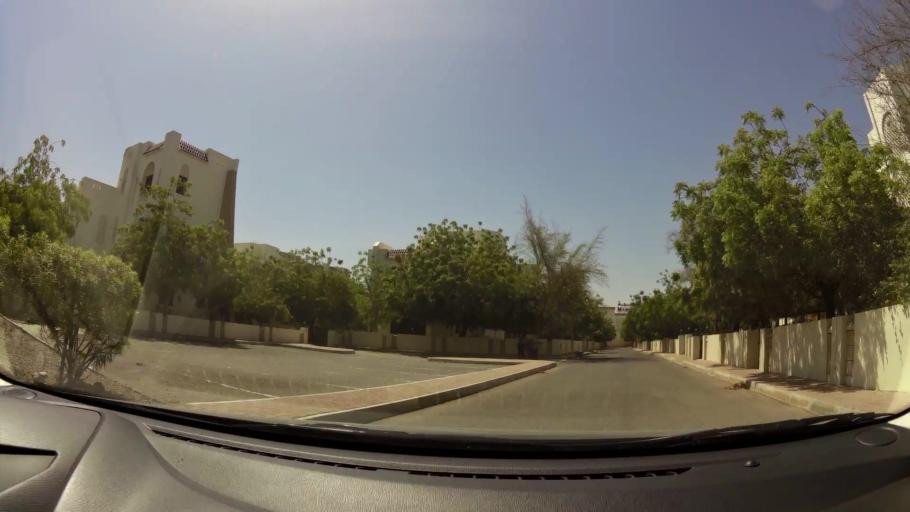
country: OM
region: Muhafazat Masqat
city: As Sib al Jadidah
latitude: 23.6154
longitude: 58.2451
